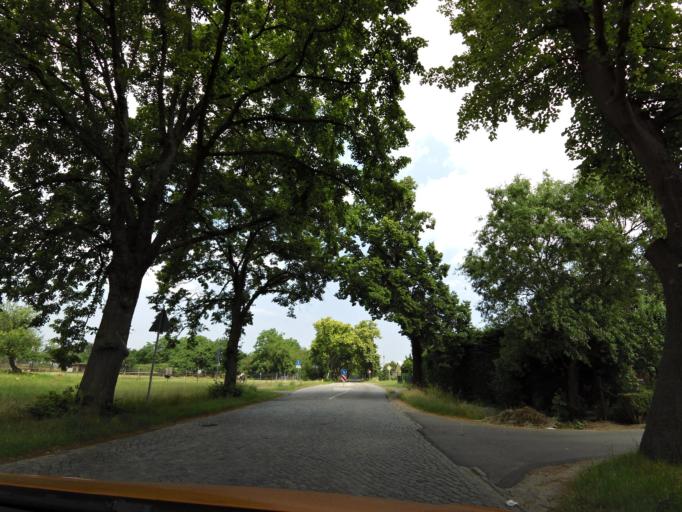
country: DE
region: Brandenburg
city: Nauen
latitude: 52.5814
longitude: 12.8748
